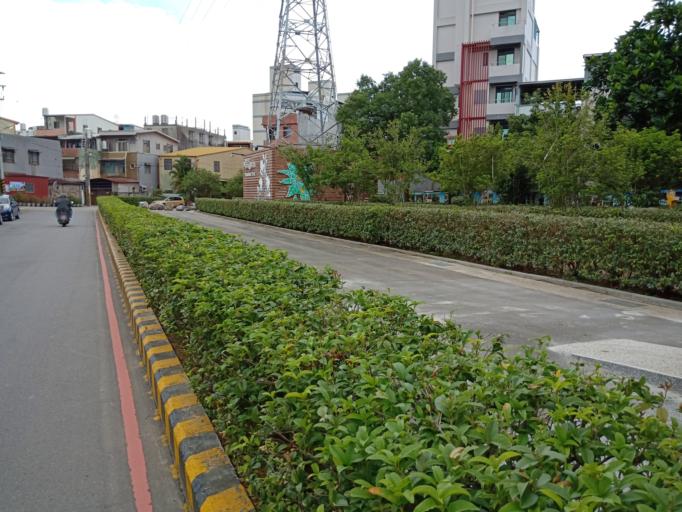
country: TW
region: Taiwan
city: Taoyuan City
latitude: 24.9495
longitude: 121.2631
